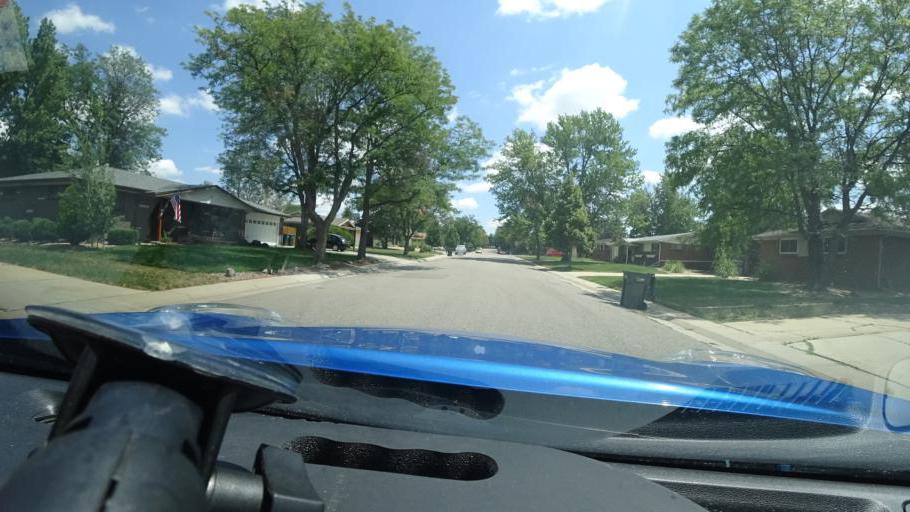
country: US
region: Colorado
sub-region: Adams County
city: Aurora
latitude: 39.7043
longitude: -104.8400
